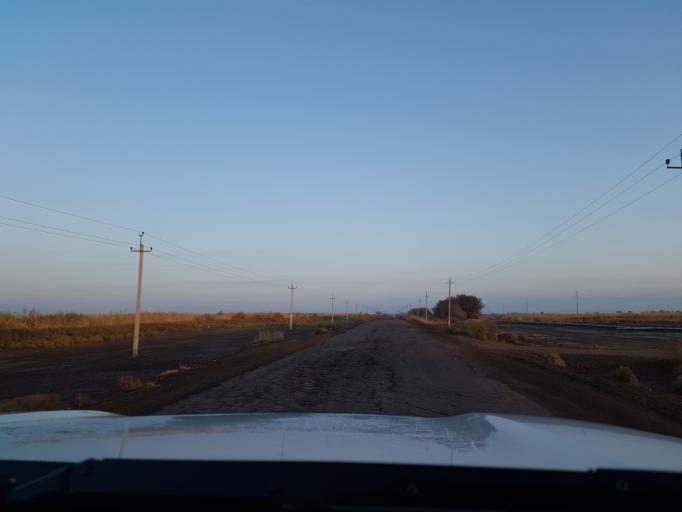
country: TM
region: Dasoguz
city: Koeneuergench
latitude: 41.8324
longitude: 58.7043
